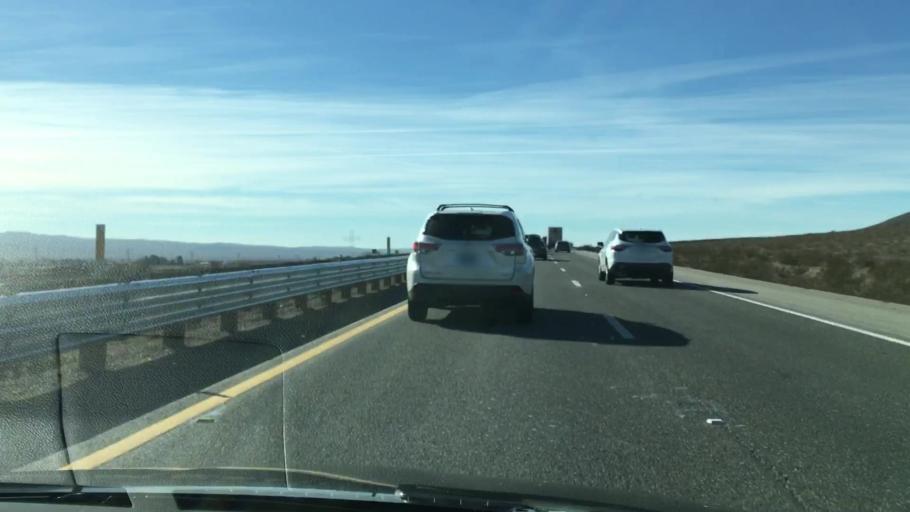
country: US
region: California
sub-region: San Bernardino County
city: Barstow
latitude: 34.9155
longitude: -116.7848
